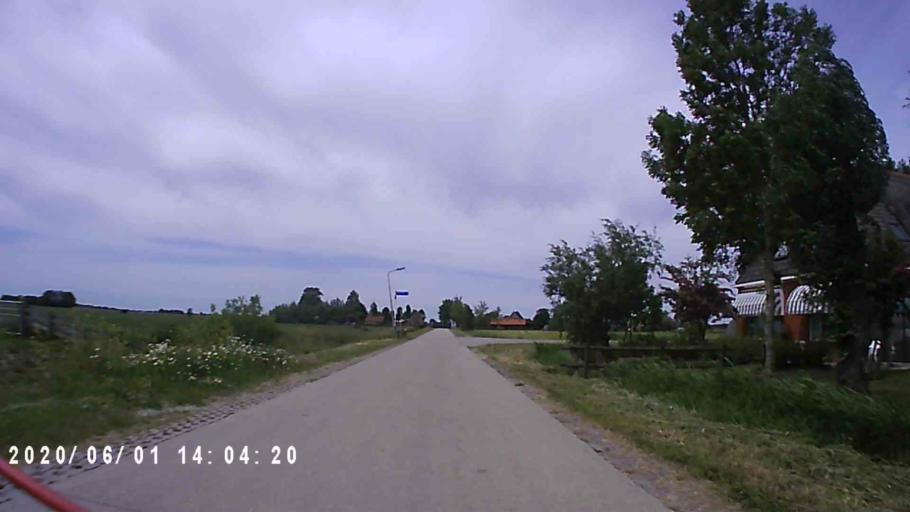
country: NL
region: Friesland
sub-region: Gemeente Littenseradiel
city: Winsum
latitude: 53.1142
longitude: 5.6324
